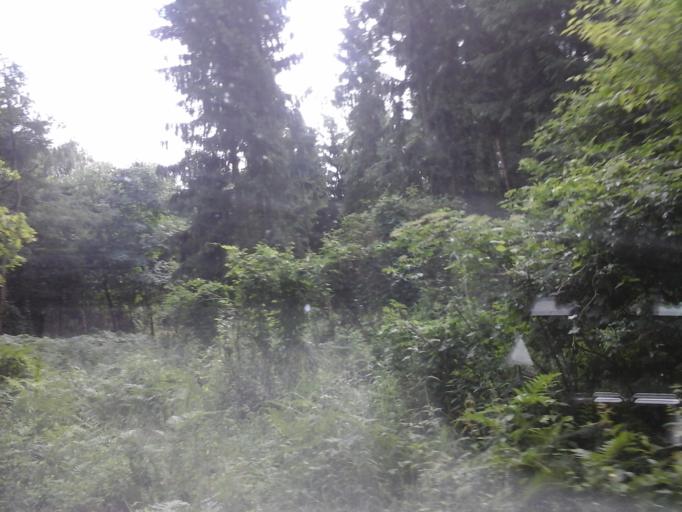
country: PL
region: West Pomeranian Voivodeship
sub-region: Powiat choszczenski
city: Krzecin
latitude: 53.0500
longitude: 15.4546
